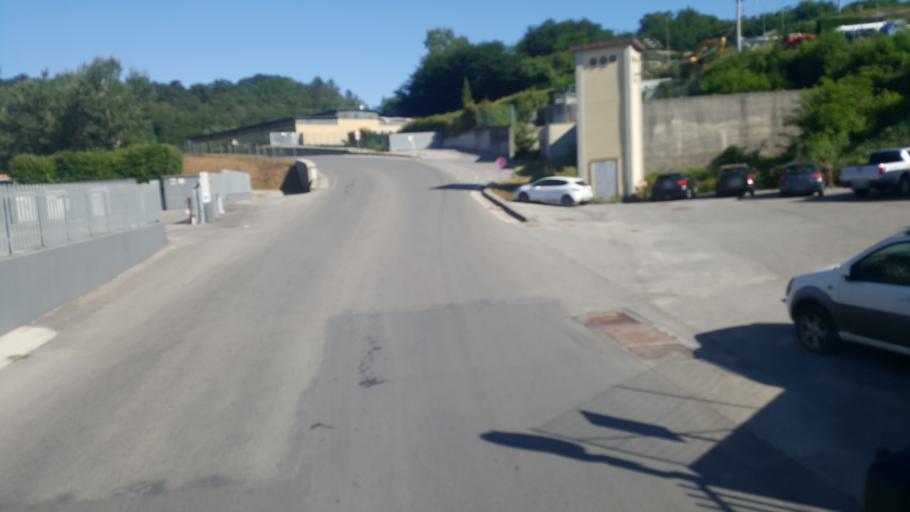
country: IT
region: Tuscany
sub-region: Provincia di Lucca
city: Castelnuovo di Garfagnana
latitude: 44.1218
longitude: 10.3974
